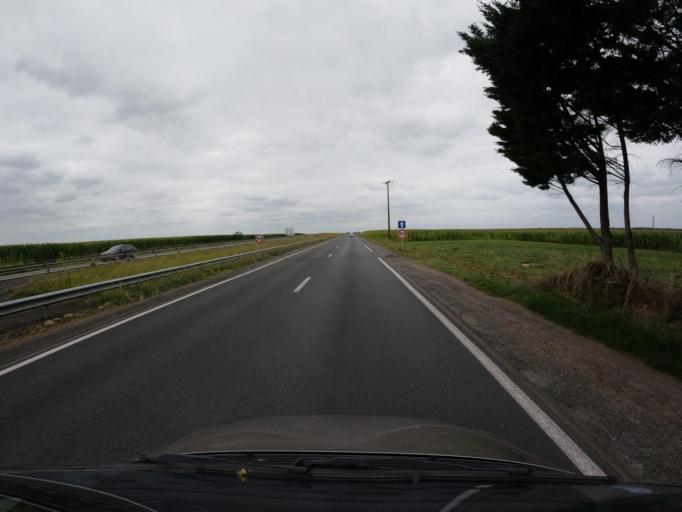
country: FR
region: Pays de la Loire
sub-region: Departement de la Vendee
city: Maillezais
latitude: 46.4225
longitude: -0.7121
